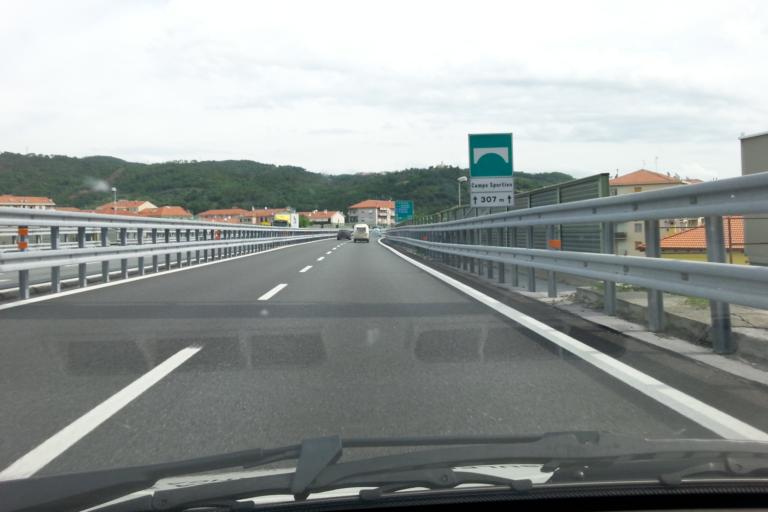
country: IT
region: Liguria
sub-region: Provincia di Savona
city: Valleggia
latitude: 44.2799
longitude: 8.4295
